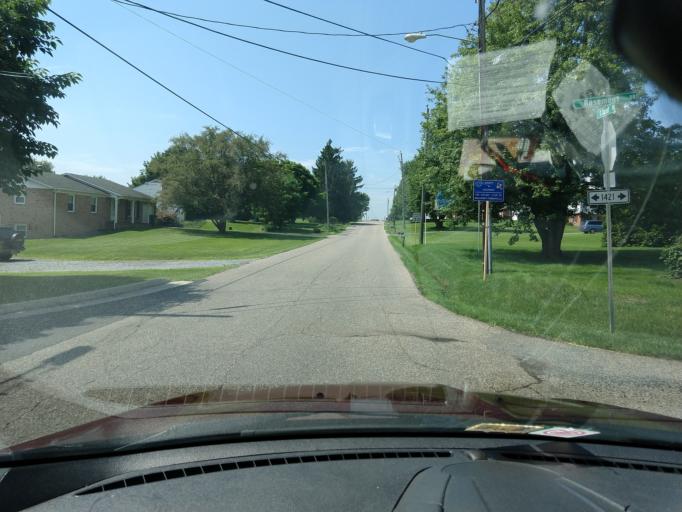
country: US
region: Virginia
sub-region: Rockingham County
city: Broadway
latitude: 38.6089
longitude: -78.8113
